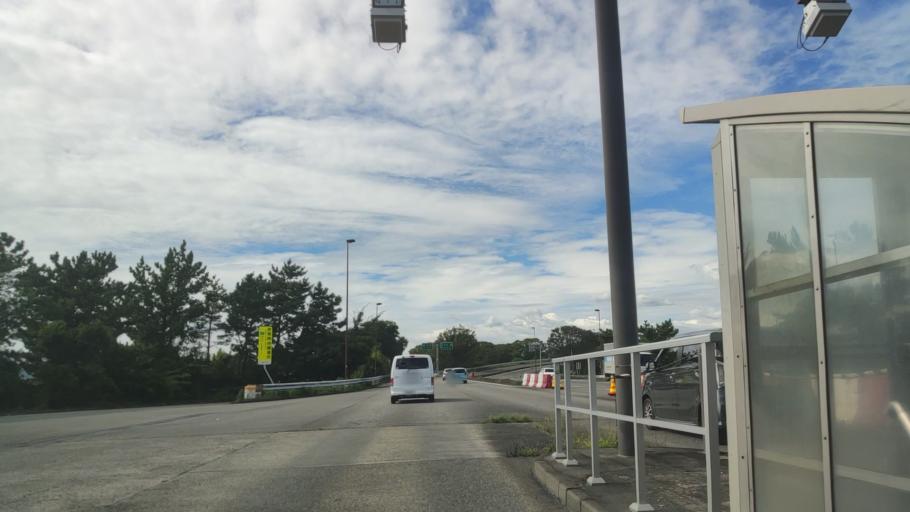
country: JP
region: Shizuoka
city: Hamamatsu
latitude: 34.7630
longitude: 137.6810
